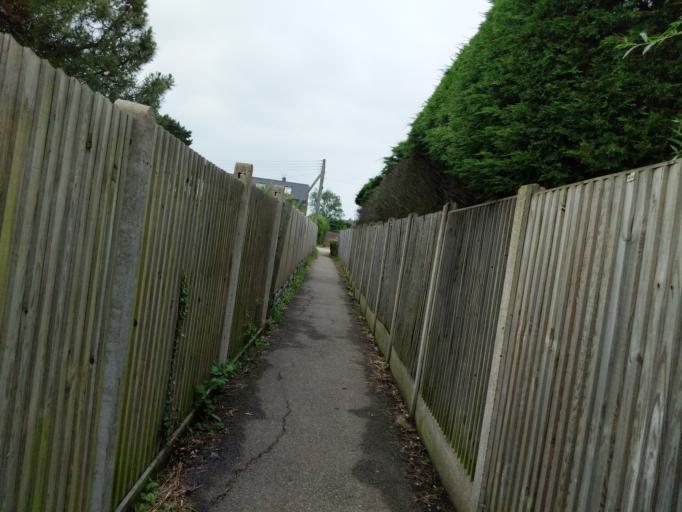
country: GB
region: England
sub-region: Kent
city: Whitstable
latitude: 51.3456
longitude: 1.0058
